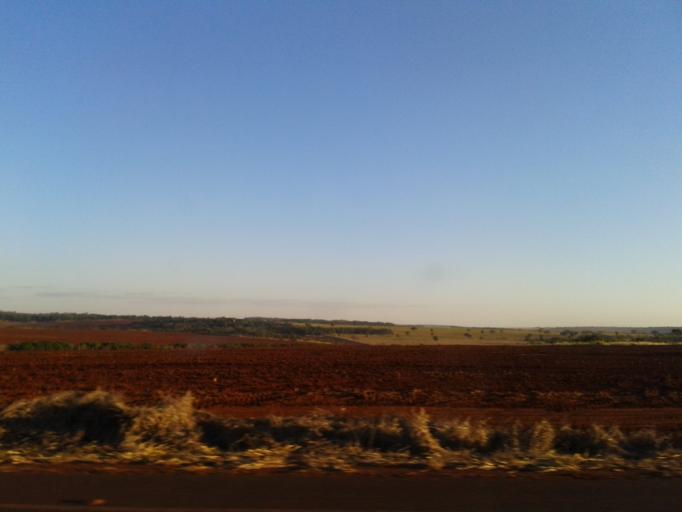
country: BR
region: Minas Gerais
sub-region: Centralina
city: Centralina
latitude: -18.7261
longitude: -49.2725
